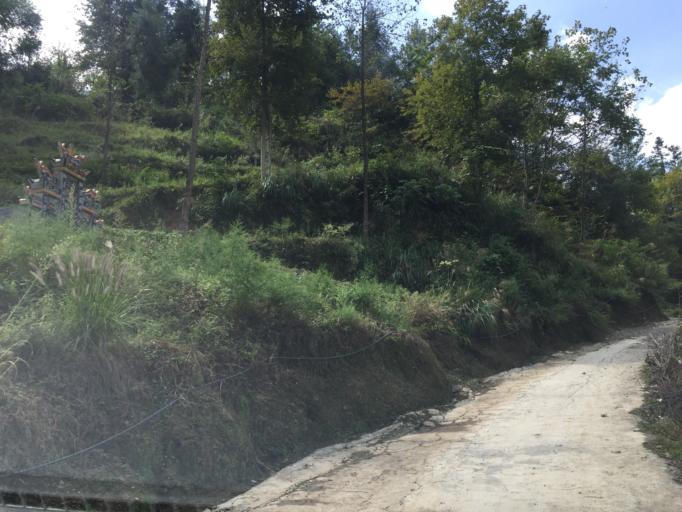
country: CN
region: Guizhou Sheng
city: Quankou
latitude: 28.5353
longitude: 108.1177
